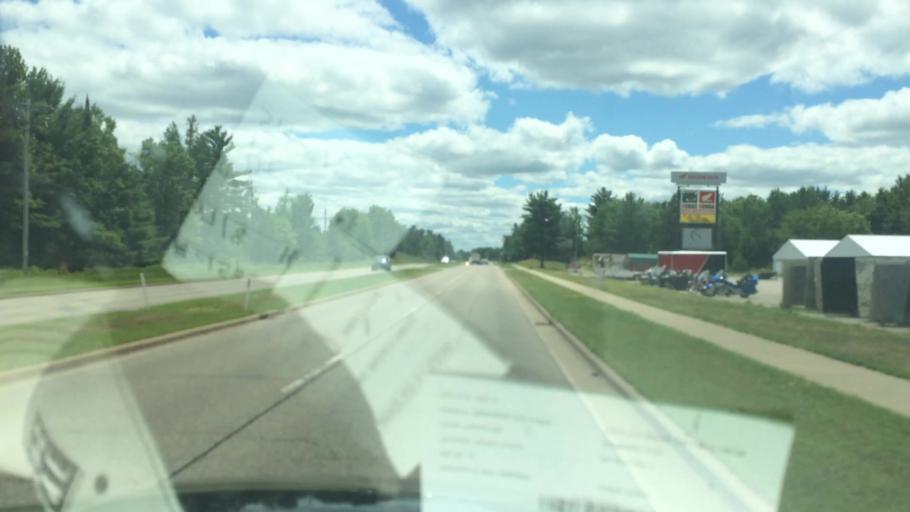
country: US
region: Wisconsin
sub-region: Oneida County
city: Rhinelander
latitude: 45.6540
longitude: -89.3817
